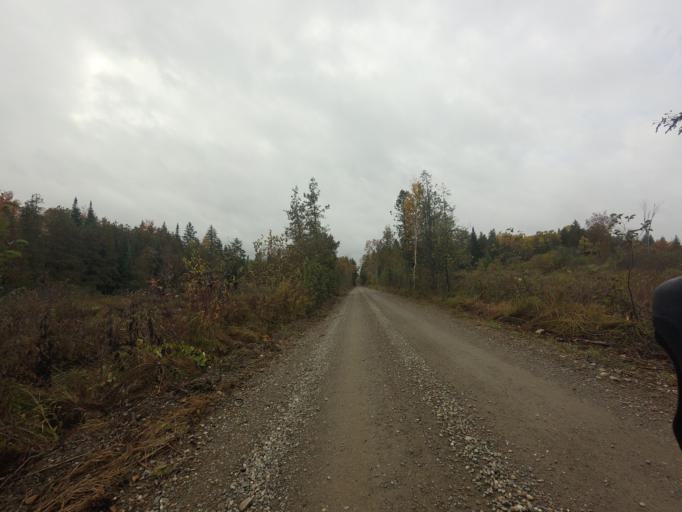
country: CA
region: Ontario
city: Renfrew
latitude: 45.1611
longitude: -76.6851
